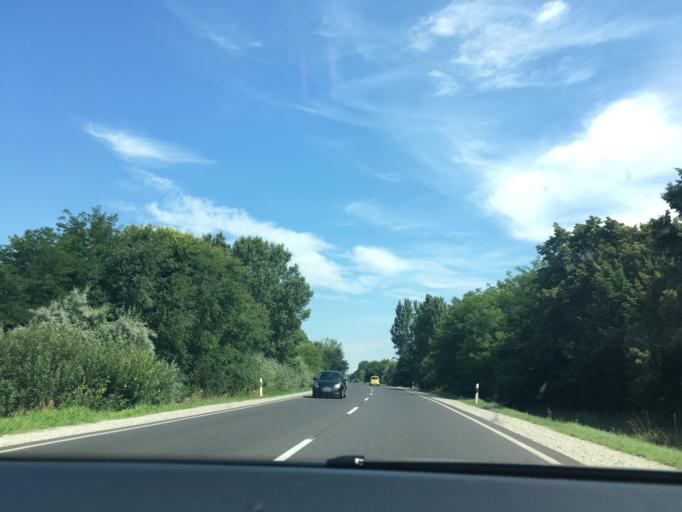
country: HU
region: Szabolcs-Szatmar-Bereg
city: Ujfeherto
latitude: 47.8386
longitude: 21.7046
